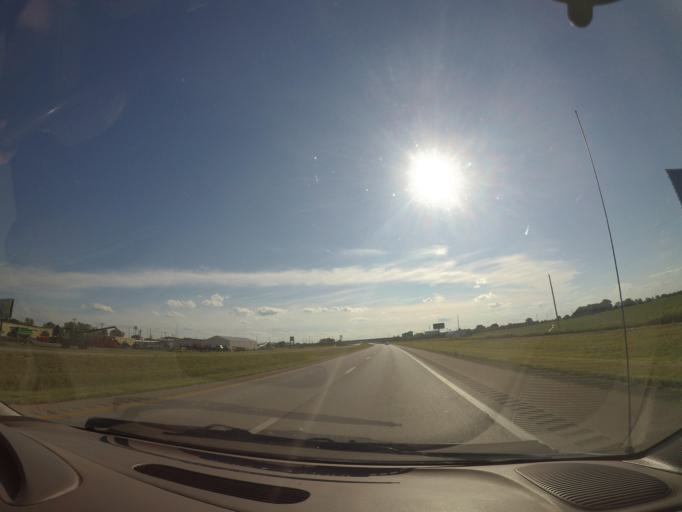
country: US
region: Ohio
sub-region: Henry County
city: Napoleon
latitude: 41.4167
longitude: -84.0902
